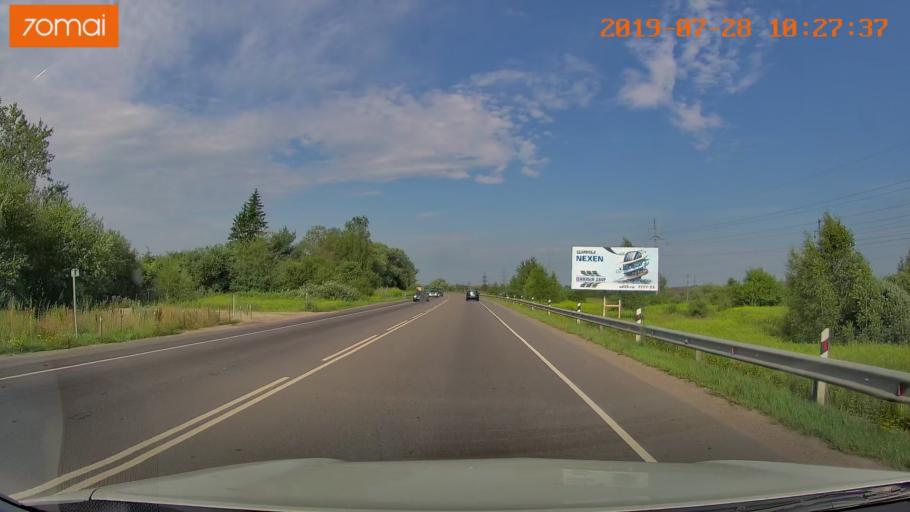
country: RU
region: Kaliningrad
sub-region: Gorod Kaliningrad
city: Kaliningrad
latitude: 54.7712
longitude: 20.5141
